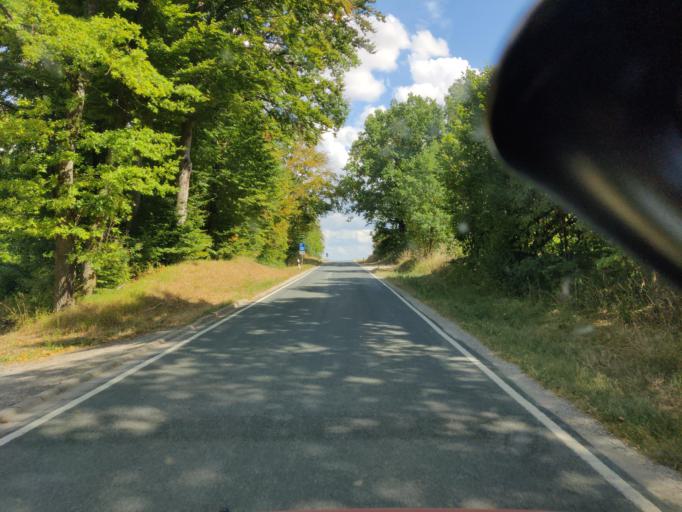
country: DE
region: Bavaria
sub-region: Regierungsbezirk Mittelfranken
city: Thalmassing
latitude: 49.0719
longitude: 11.2134
